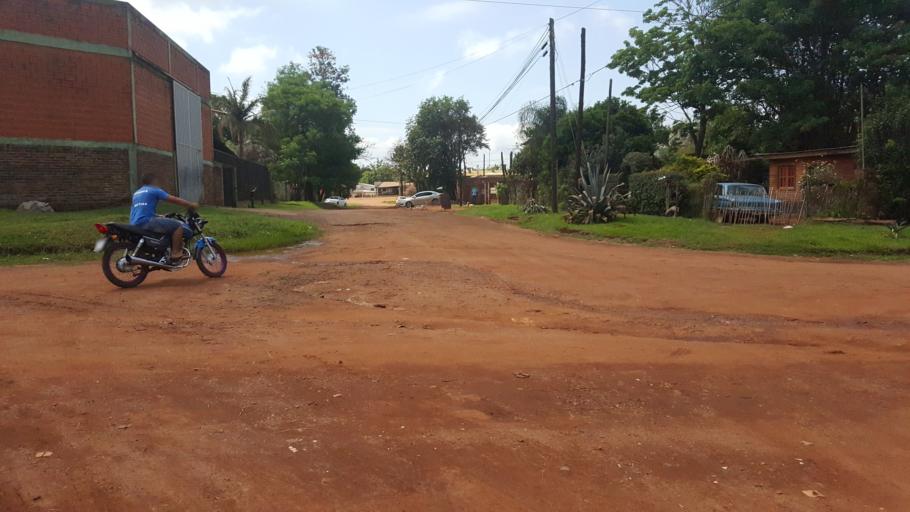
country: AR
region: Misiones
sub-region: Departamento de Capital
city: Posadas
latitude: -27.4261
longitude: -55.8980
